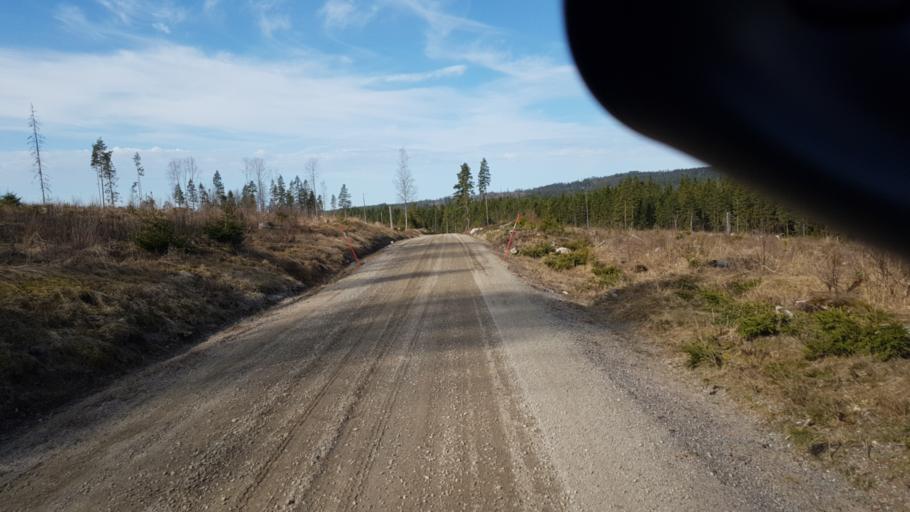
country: SE
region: Vaermland
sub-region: Arvika Kommun
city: Arvika
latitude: 59.5410
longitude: 12.4273
